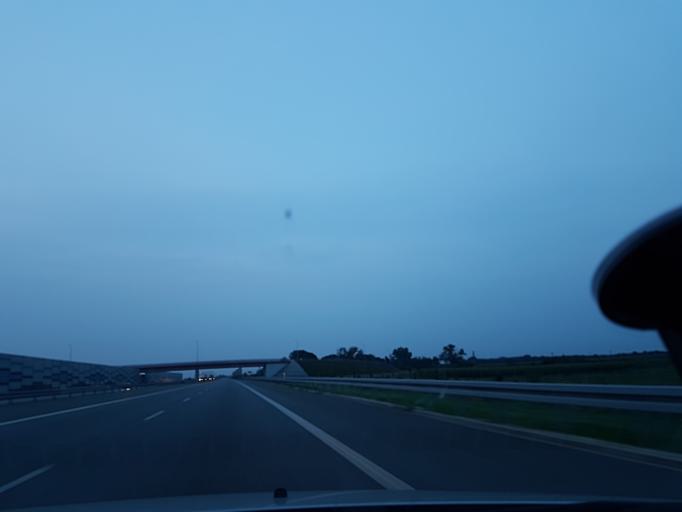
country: PL
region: Lodz Voivodeship
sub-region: Powiat leczycki
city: Piatek
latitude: 52.0493
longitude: 19.5371
